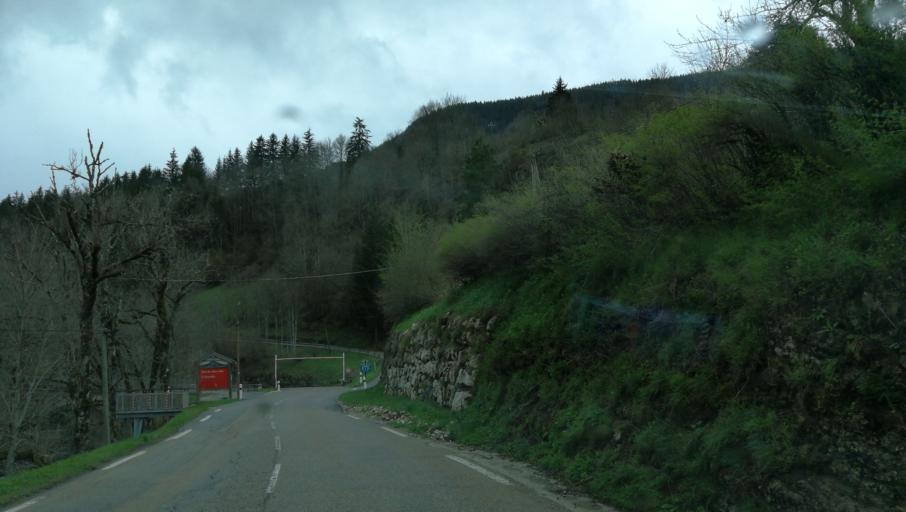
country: FR
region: Rhone-Alpes
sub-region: Departement de l'Isere
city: Villard-de-Lans
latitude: 45.0853
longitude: 5.5214
